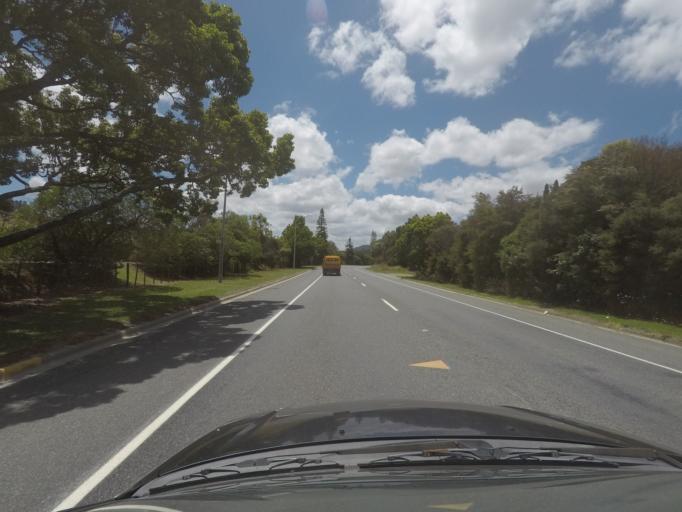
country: NZ
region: Northland
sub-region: Whangarei
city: Whangarei
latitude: -35.7483
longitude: 174.3207
